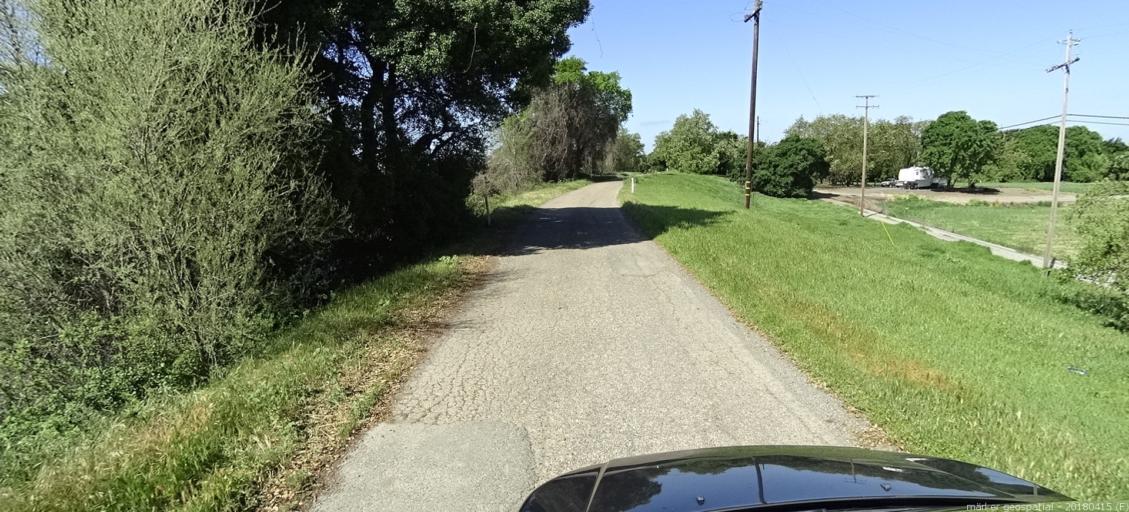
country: US
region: California
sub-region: Solano County
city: Rio Vista
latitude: 38.1241
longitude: -121.6670
